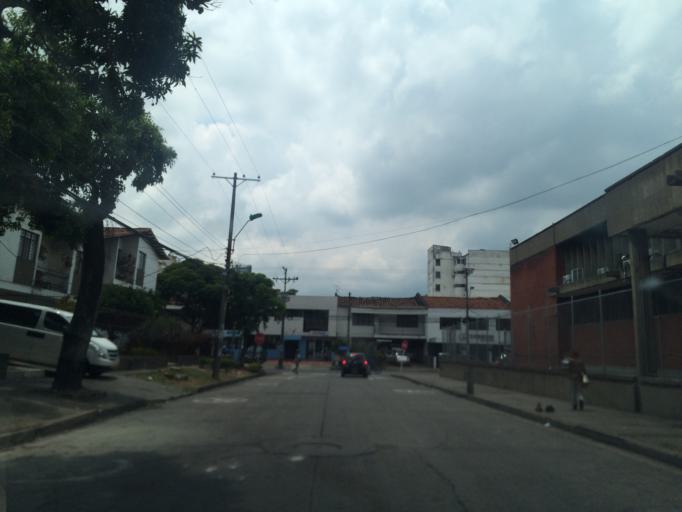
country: CO
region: Valle del Cauca
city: Cali
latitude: 3.4677
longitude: -76.5251
